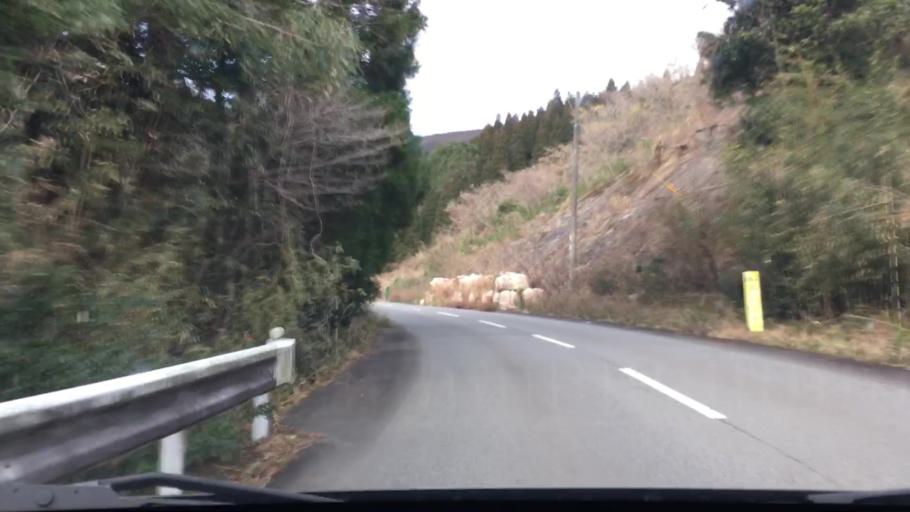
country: JP
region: Miyazaki
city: Nichinan
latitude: 31.6595
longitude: 131.3249
